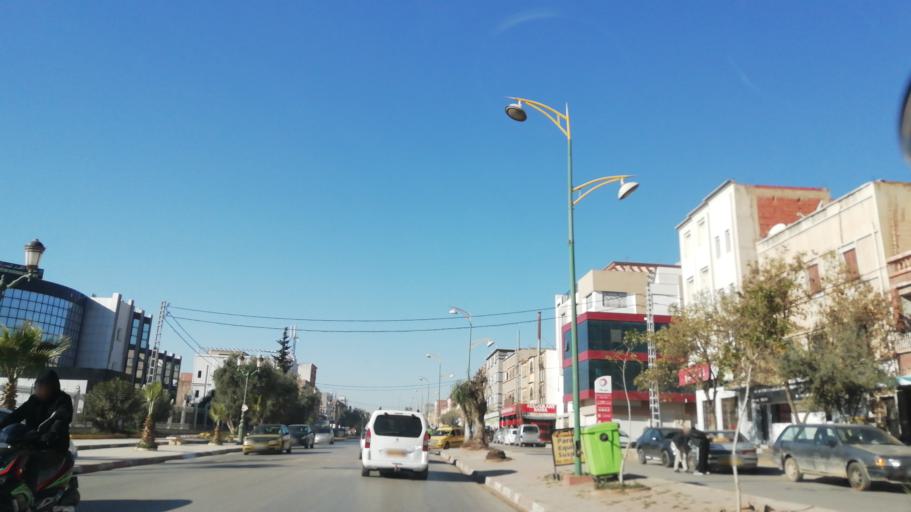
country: DZ
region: Tlemcen
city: Nedroma
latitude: 34.8453
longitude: -1.7457
